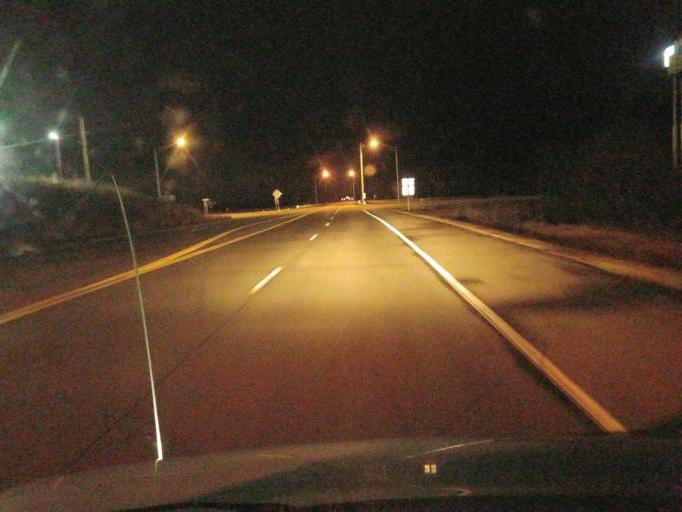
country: US
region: Missouri
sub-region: Franklin County
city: Villa Ridge
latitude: 38.4749
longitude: -90.8523
